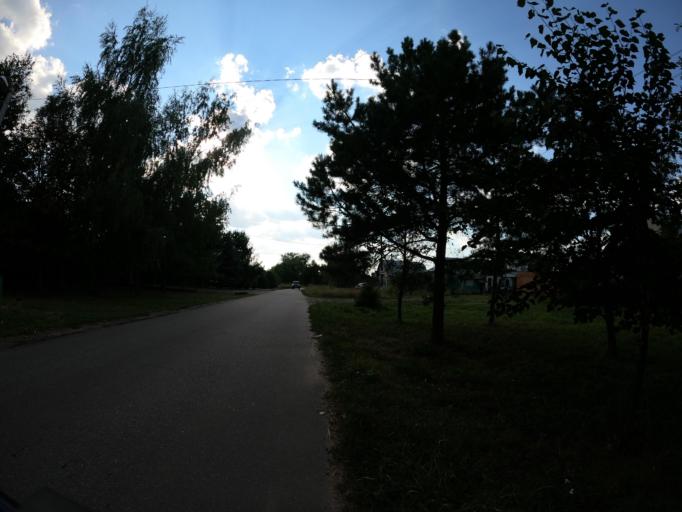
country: RU
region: Moskovskaya
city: Raduzhnyy
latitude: 55.1722
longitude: 38.7252
